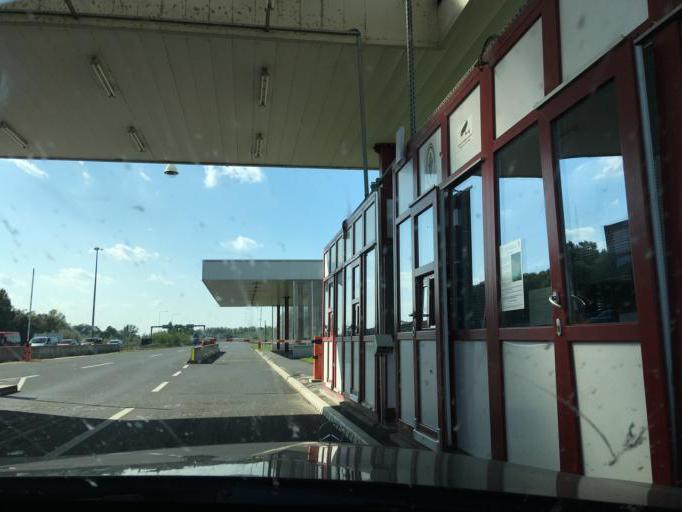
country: HU
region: Zala
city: Letenye
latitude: 46.4125
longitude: 16.7132
